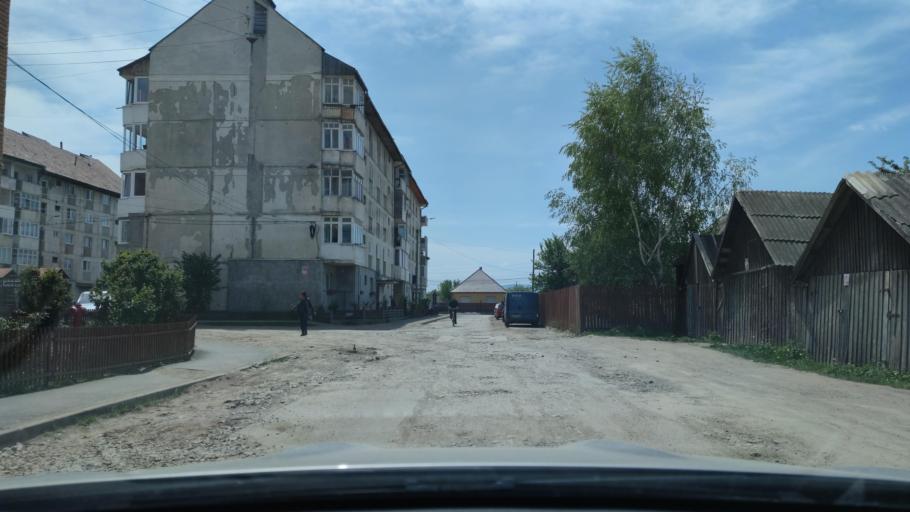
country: RO
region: Harghita
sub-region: Municipiul Gheorgheni
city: Gheorgheni
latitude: 46.7196
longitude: 25.5871
